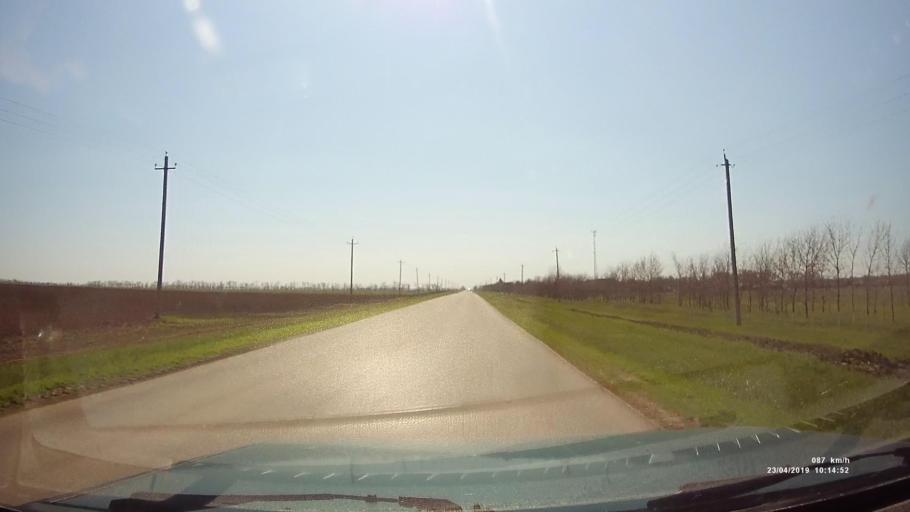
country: RU
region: Rostov
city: Sovetskoye
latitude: 46.6724
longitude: 42.3750
